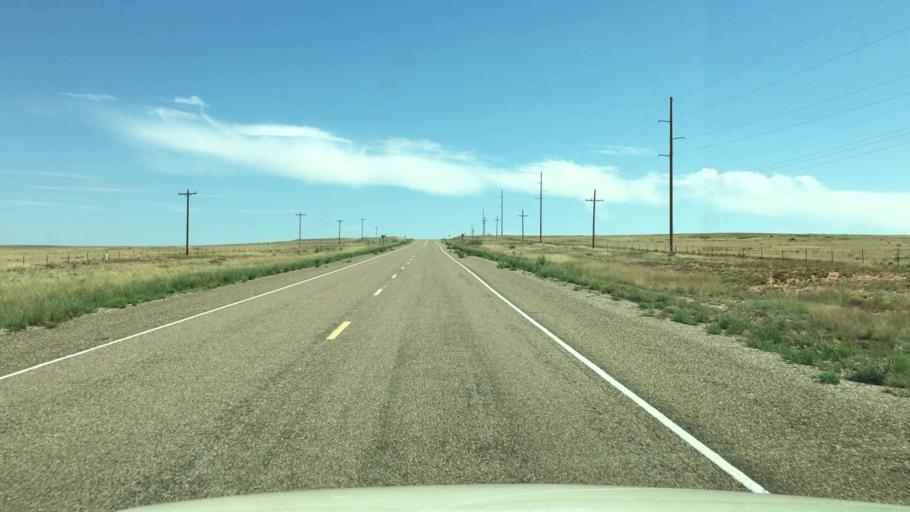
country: US
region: New Mexico
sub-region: Chaves County
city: Roswell
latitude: 33.9333
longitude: -104.5959
